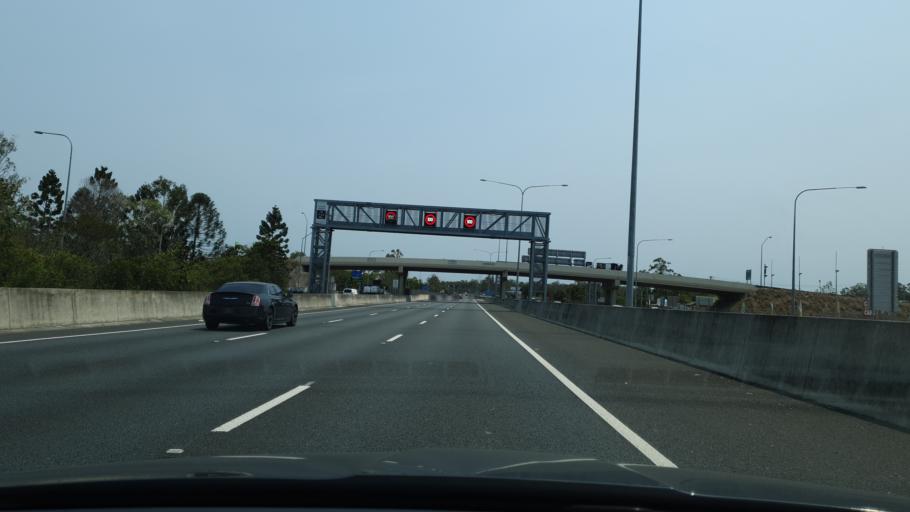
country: AU
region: Queensland
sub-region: Brisbane
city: Wacol
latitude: -27.5877
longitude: 152.9276
